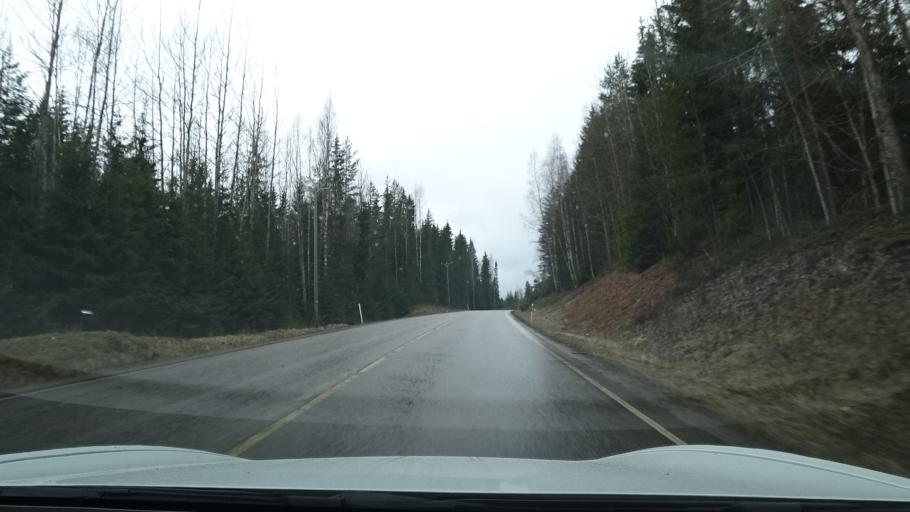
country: FI
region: Uusimaa
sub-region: Porvoo
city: Pukkila
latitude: 60.7689
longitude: 25.4874
